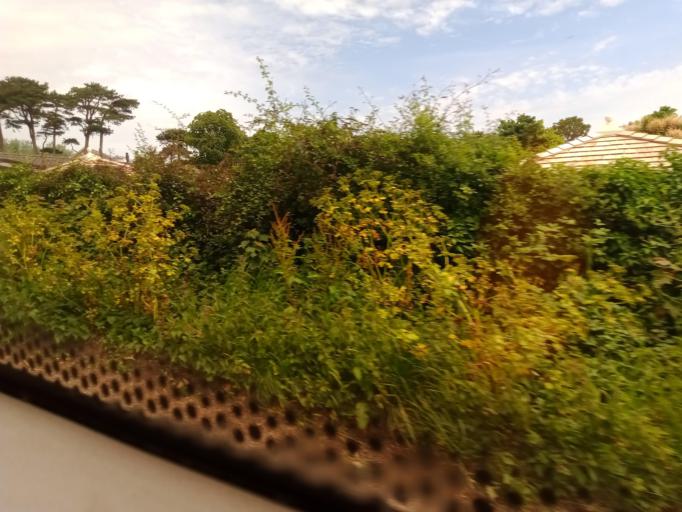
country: GB
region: Wales
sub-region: Anglesey
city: Llangoed
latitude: 53.2930
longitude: -4.0699
